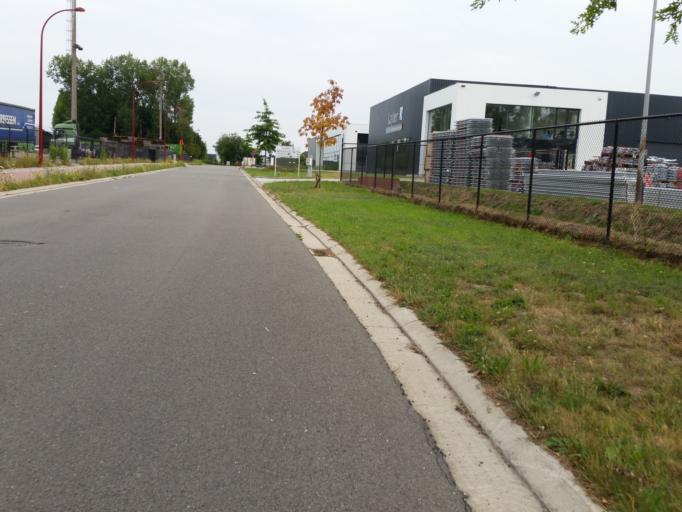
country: BE
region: Flanders
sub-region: Provincie Antwerpen
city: Kontich
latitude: 51.1061
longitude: 4.4475
